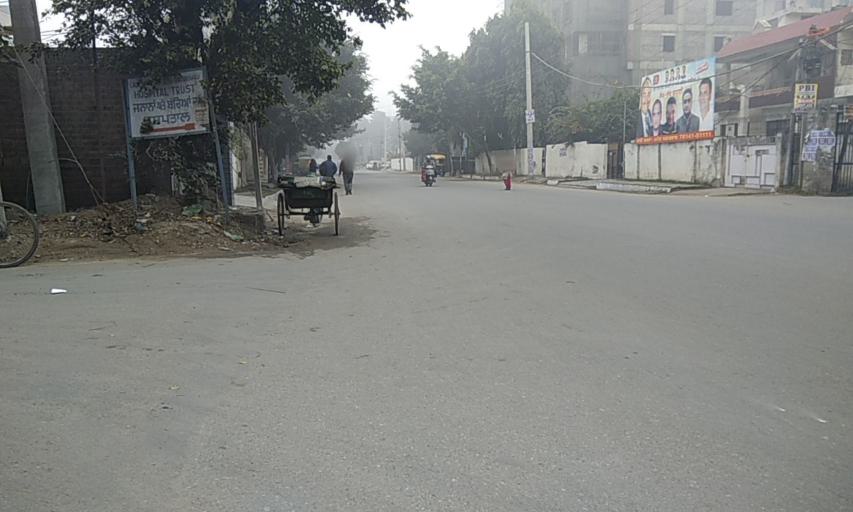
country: IN
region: Punjab
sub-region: Amritsar
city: Amritsar
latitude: 31.6399
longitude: 74.8665
